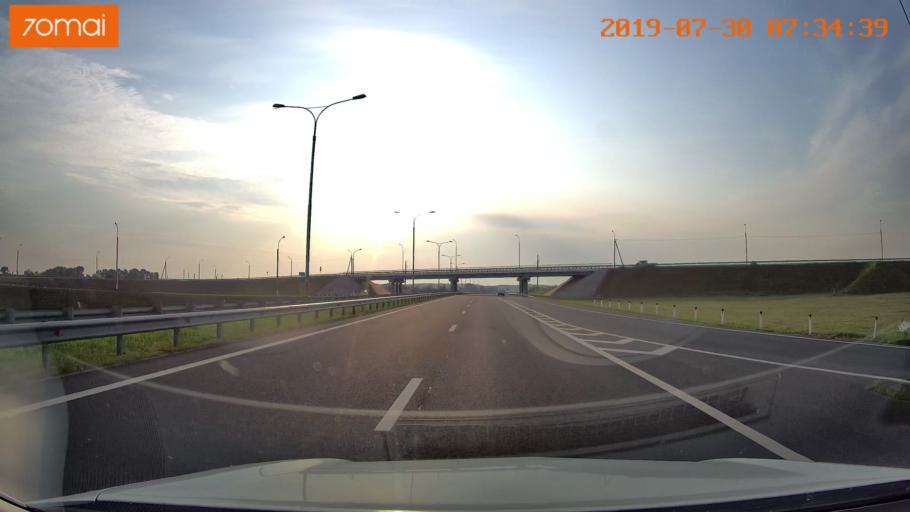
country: RU
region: Kaliningrad
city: Gvardeysk
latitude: 54.6723
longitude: 21.0783
